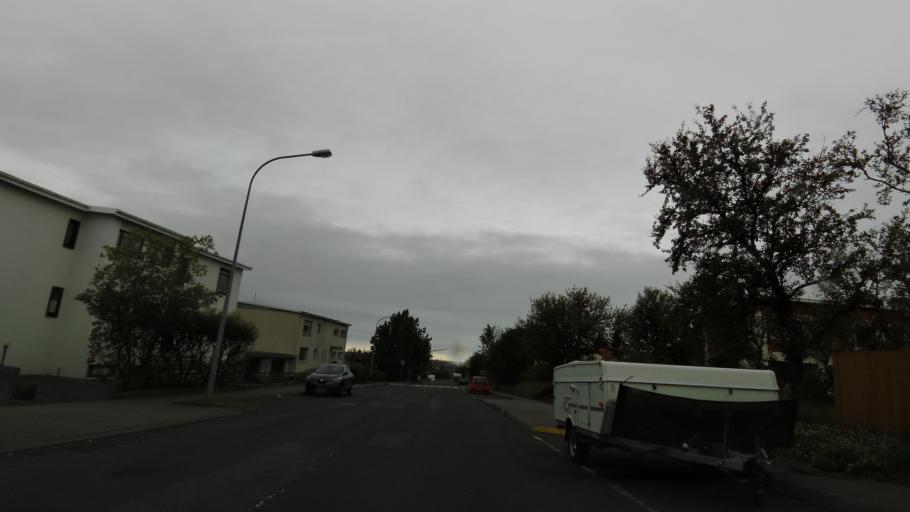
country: IS
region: Capital Region
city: Kopavogur
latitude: 64.1080
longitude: -21.8990
